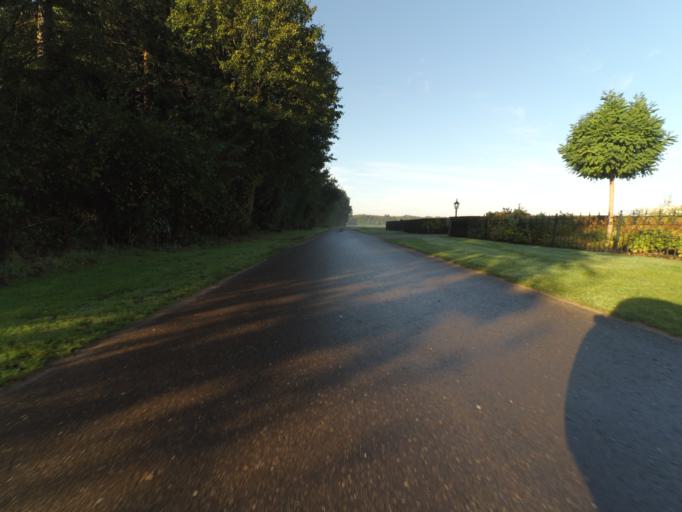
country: NL
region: Gelderland
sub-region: Gemeente Apeldoorn
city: Uddel
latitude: 52.2271
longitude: 5.7639
